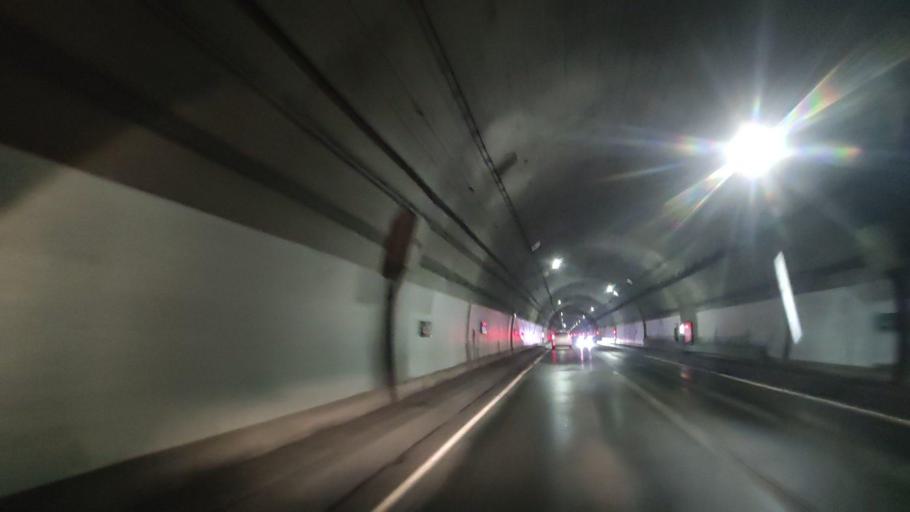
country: JP
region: Hokkaido
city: Rumoi
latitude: 43.7073
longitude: 141.3340
